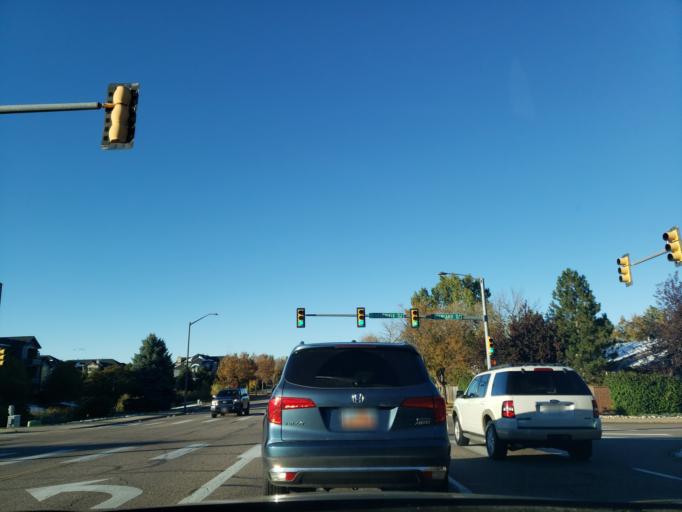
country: US
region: Colorado
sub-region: Larimer County
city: Fort Collins
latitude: 40.5140
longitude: -105.0581
